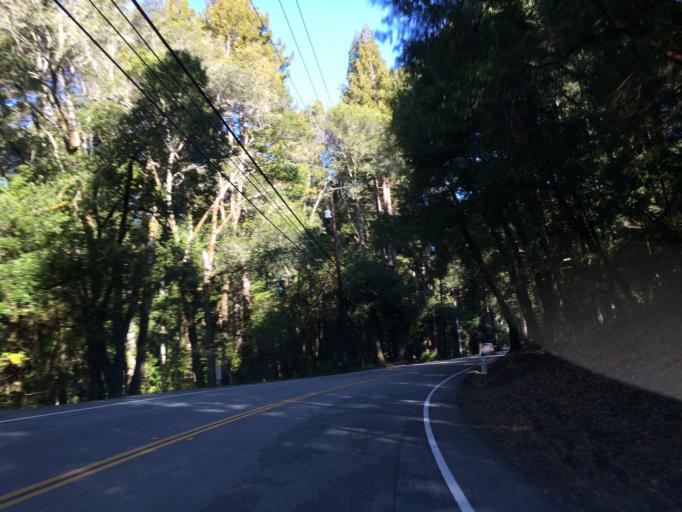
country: US
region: California
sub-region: Santa Cruz County
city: Boulder Creek
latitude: 37.1810
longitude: -122.1409
